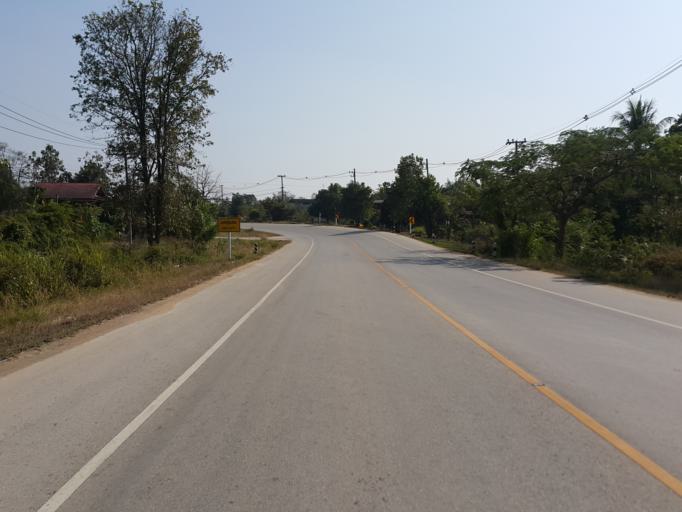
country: TH
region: Lampang
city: Chae Hom
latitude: 18.7372
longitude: 99.5775
